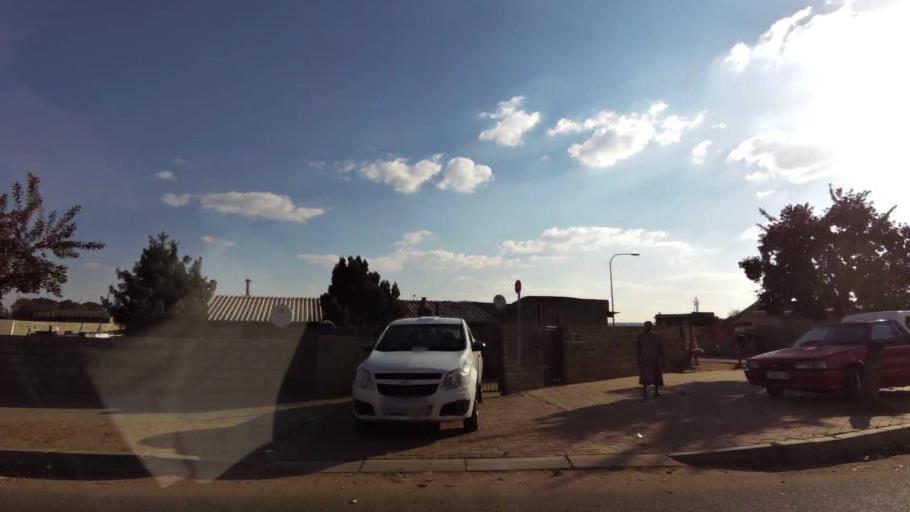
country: ZA
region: Gauteng
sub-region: City of Johannesburg Metropolitan Municipality
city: Roodepoort
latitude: -26.2095
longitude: 27.8845
